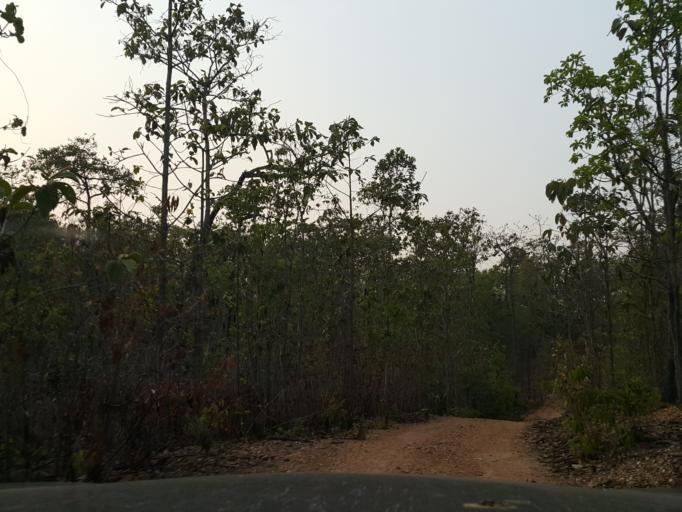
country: TH
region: Lamphun
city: Thung Hua Chang
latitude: 17.9056
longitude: 99.0817
